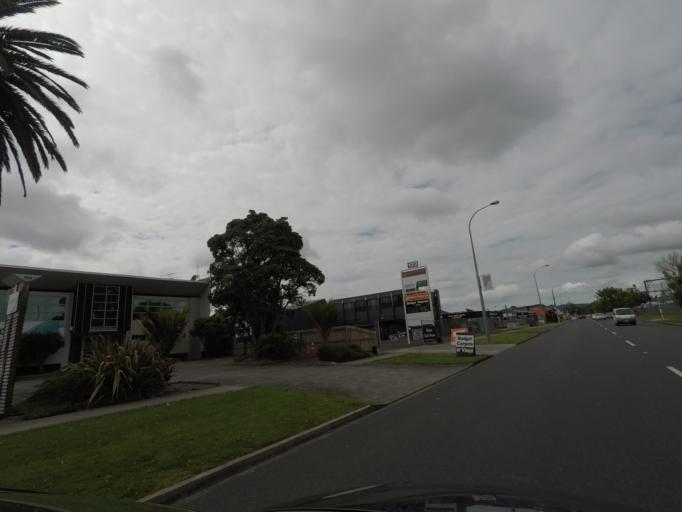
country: NZ
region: Auckland
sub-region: Auckland
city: Waitakere
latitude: -36.8881
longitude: 174.6316
